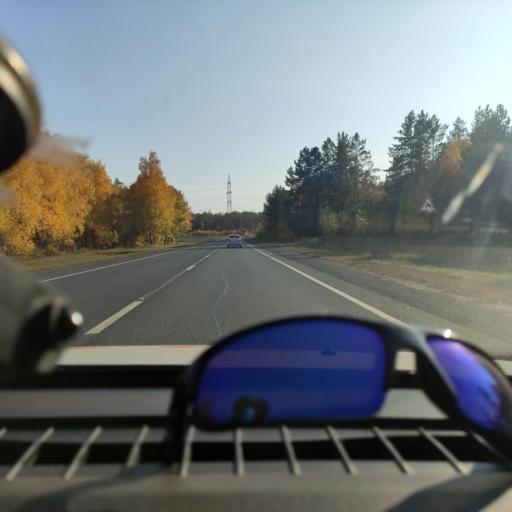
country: RU
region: Samara
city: Volzhskiy
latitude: 53.4534
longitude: 50.1261
